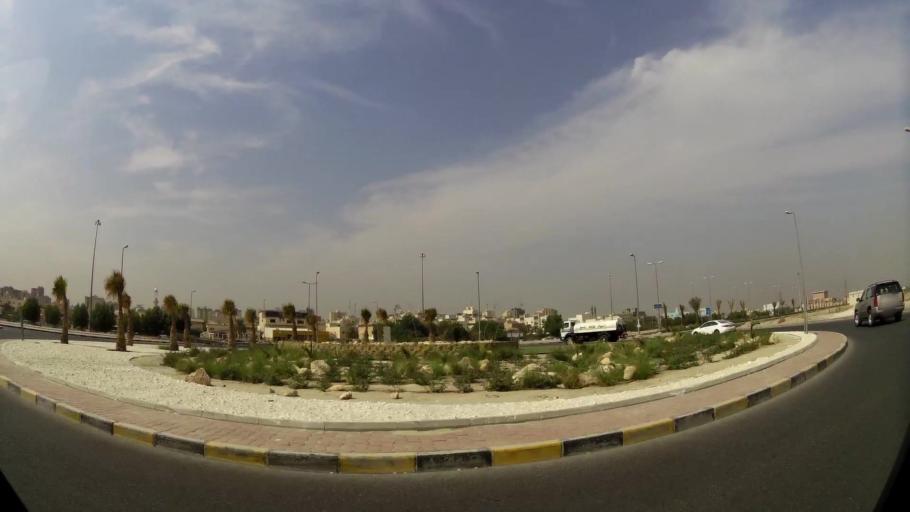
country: KW
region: Al Farwaniyah
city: Janub as Surrah
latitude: 29.2938
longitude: 47.9835
